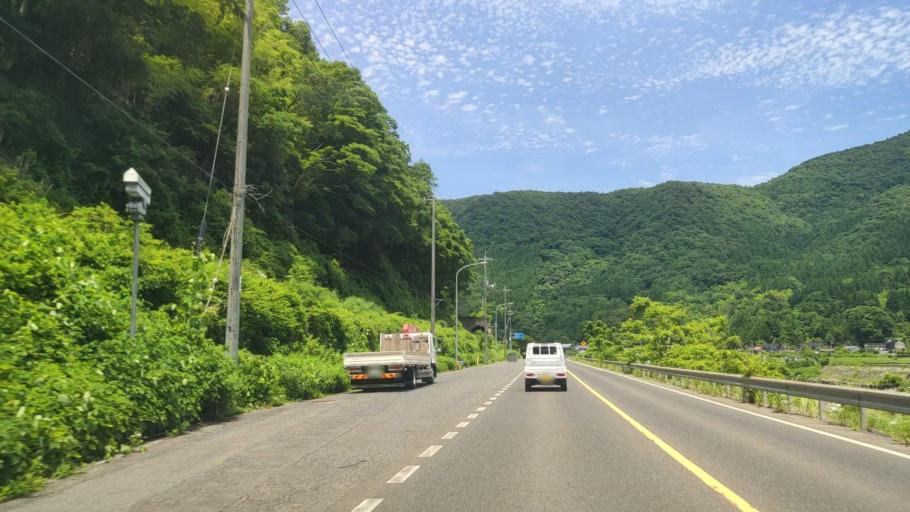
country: JP
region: Tottori
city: Tottori
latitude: 35.3639
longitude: 134.3781
